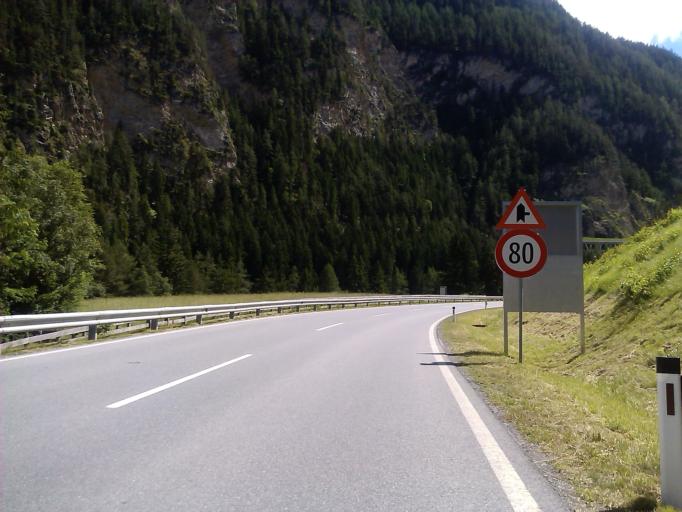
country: AT
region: Tyrol
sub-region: Politischer Bezirk Landeck
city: Pfunds
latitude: 46.9476
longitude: 10.5057
